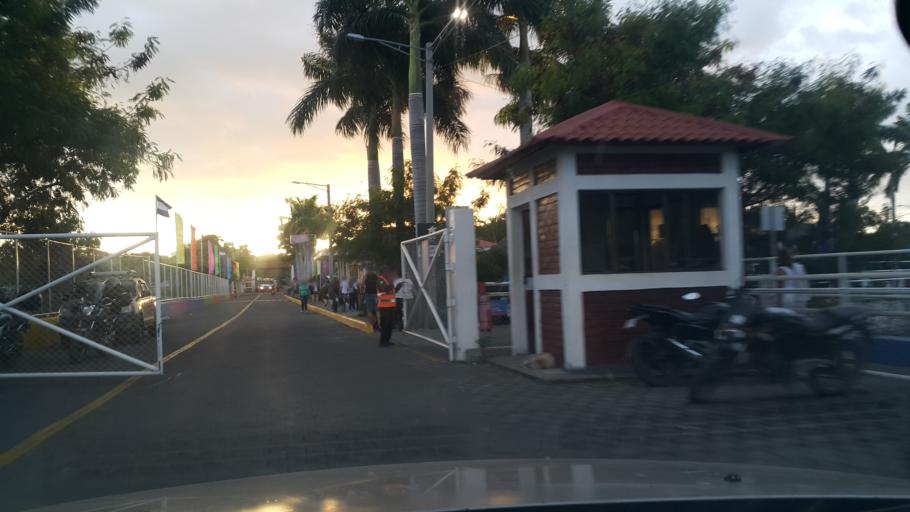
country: NI
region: Rivas
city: San Jorge
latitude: 11.4607
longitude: -85.7896
